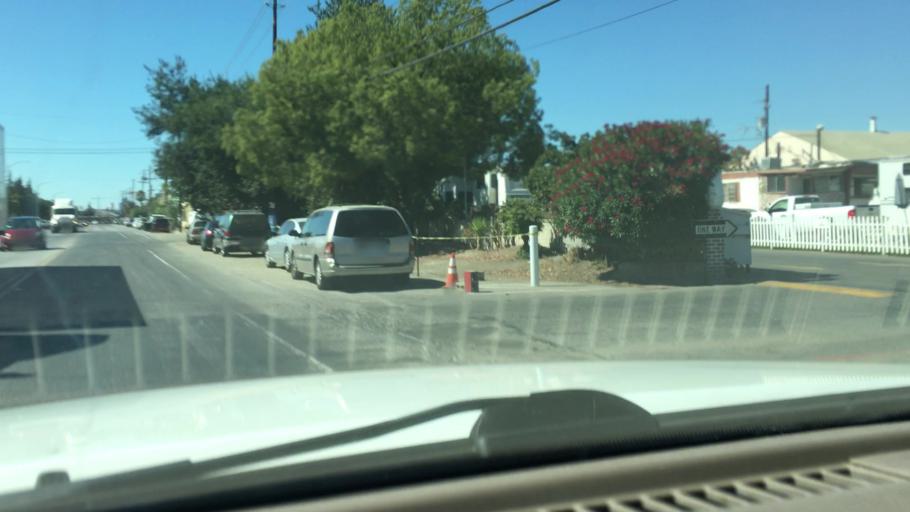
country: US
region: California
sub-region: Santa Clara County
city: Seven Trees
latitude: 37.3112
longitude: -121.8624
